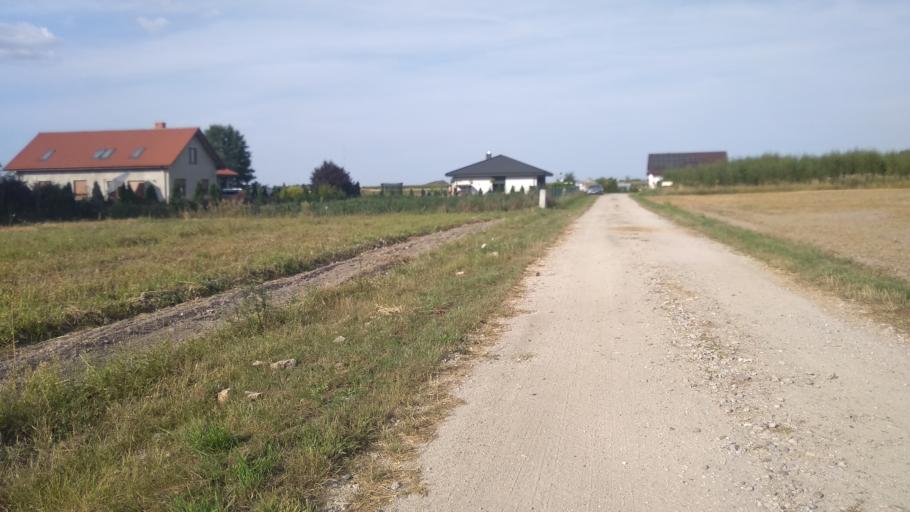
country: PL
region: Kujawsko-Pomorskie
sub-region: Powiat bydgoski
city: Osielsko
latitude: 53.2246
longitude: 18.1474
